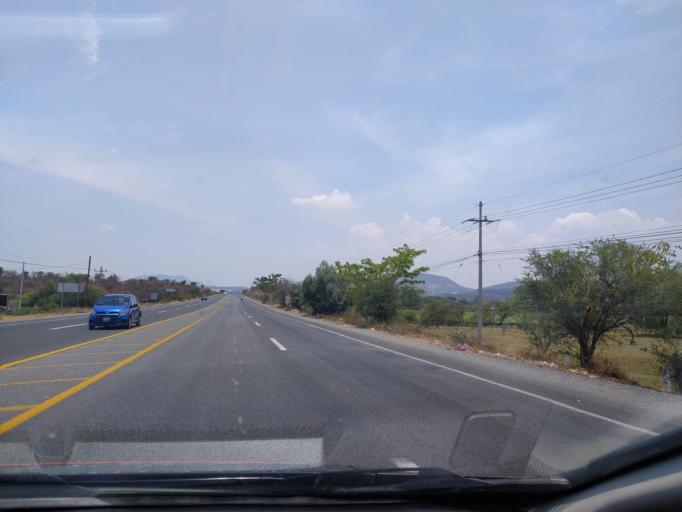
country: MX
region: Jalisco
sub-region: Acatlan de Juarez
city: Villa de los Ninos
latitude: 20.4021
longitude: -103.5936
